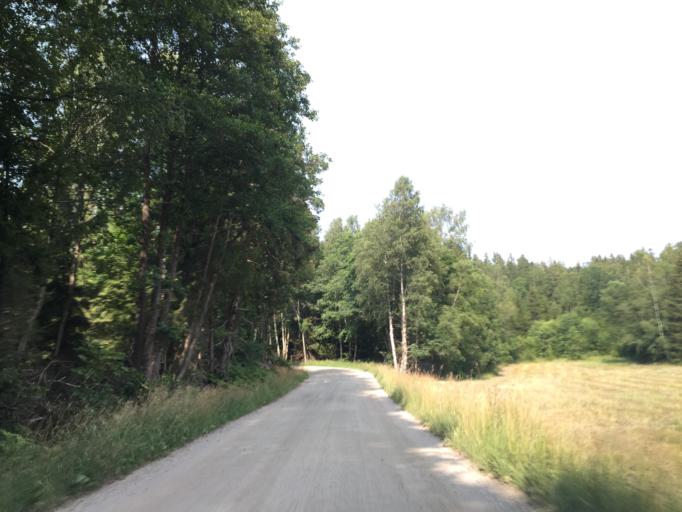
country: SE
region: Vaestra Goetaland
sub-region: Trollhattan
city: Sjuntorp
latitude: 58.2675
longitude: 12.1041
